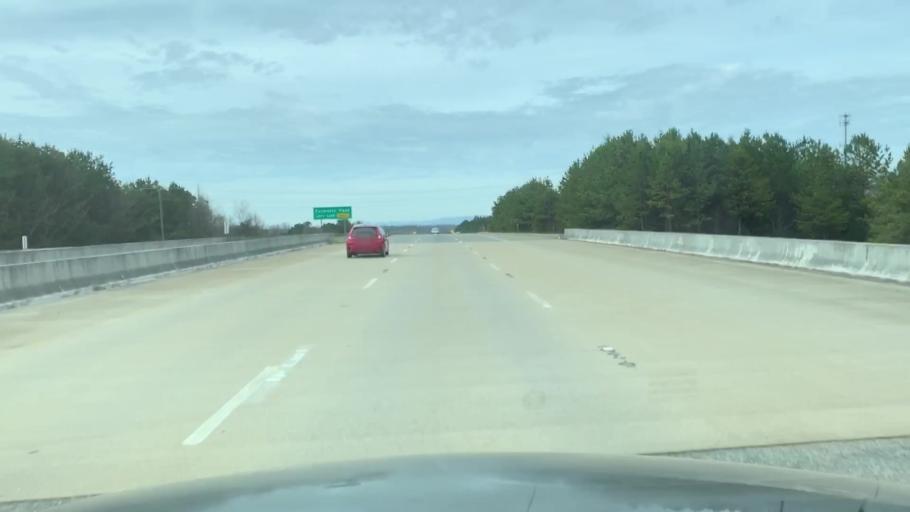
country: US
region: South Carolina
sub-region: Greenville County
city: Golden Grove
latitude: 34.7417
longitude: -82.4359
